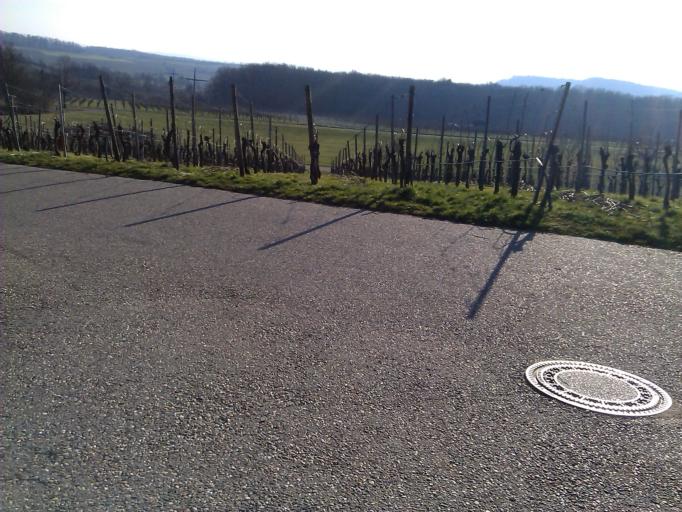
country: DE
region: Baden-Wuerttemberg
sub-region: Regierungsbezirk Stuttgart
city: Leingarten
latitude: 49.1212
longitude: 9.0963
